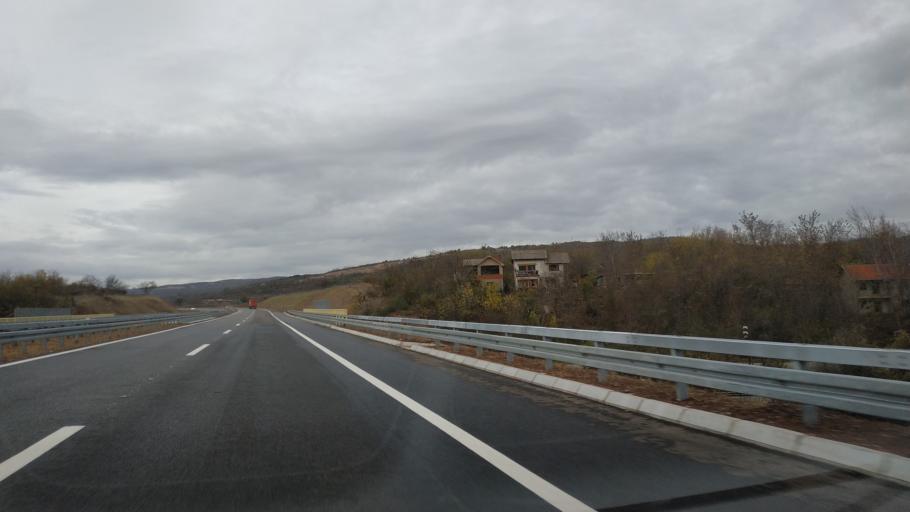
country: RS
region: Central Serbia
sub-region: Nisavski Okrug
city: Niska Banja
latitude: 43.3087
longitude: 22.0369
